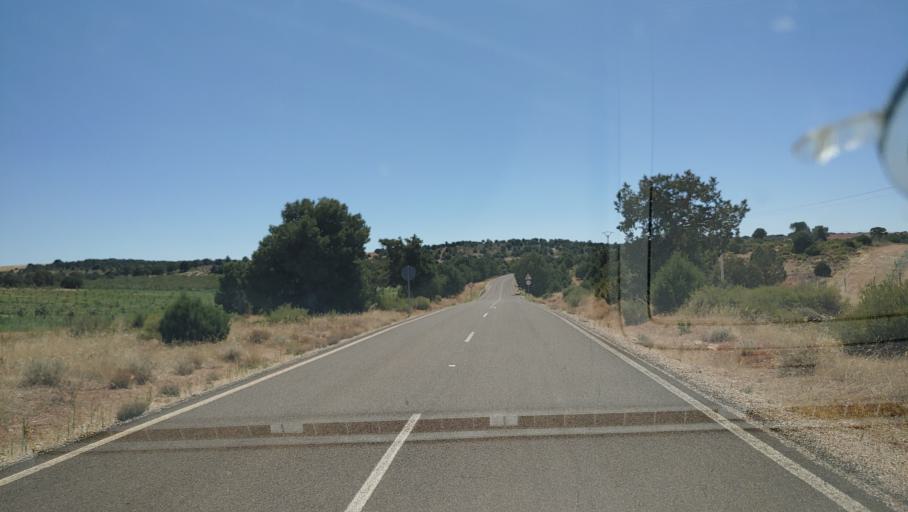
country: ES
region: Castille-La Mancha
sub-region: Provincia de Albacete
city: Ossa de Montiel
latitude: 38.8555
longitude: -2.8026
